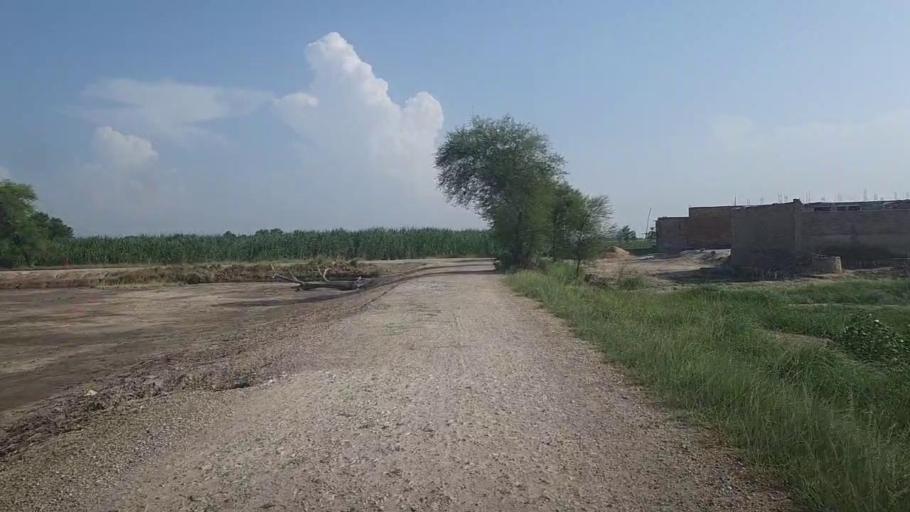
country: PK
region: Sindh
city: Ubauro
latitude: 28.1718
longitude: 69.7710
